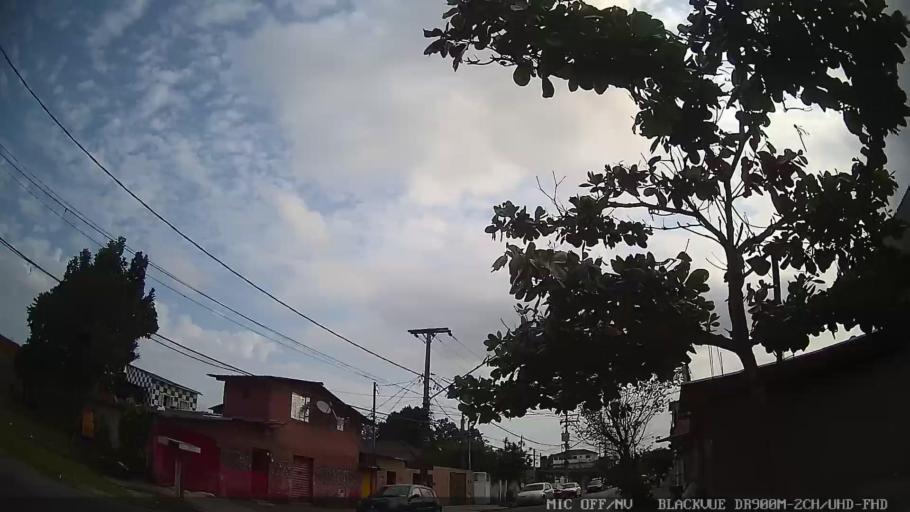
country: BR
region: Sao Paulo
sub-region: Guaruja
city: Guaruja
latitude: -23.9552
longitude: -46.2821
